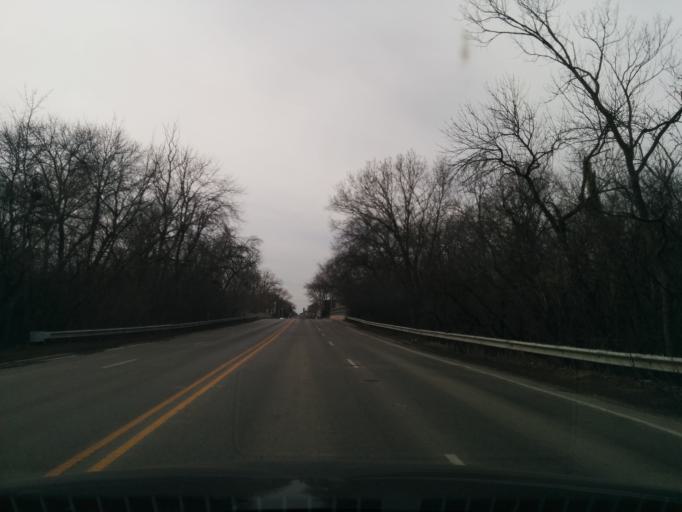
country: US
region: Illinois
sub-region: Cook County
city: Brookfield
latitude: 41.8352
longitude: -87.8411
